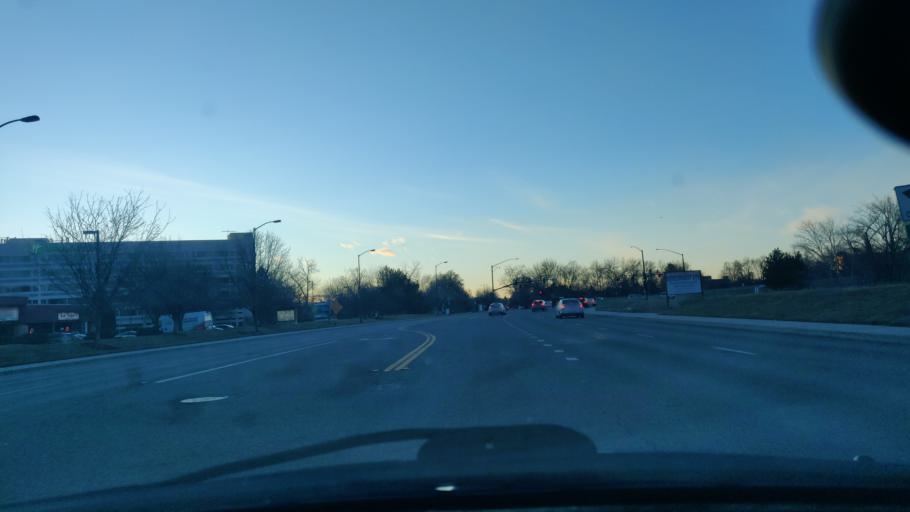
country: US
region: Idaho
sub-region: Ada County
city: Boise
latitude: 43.5987
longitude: -116.1851
